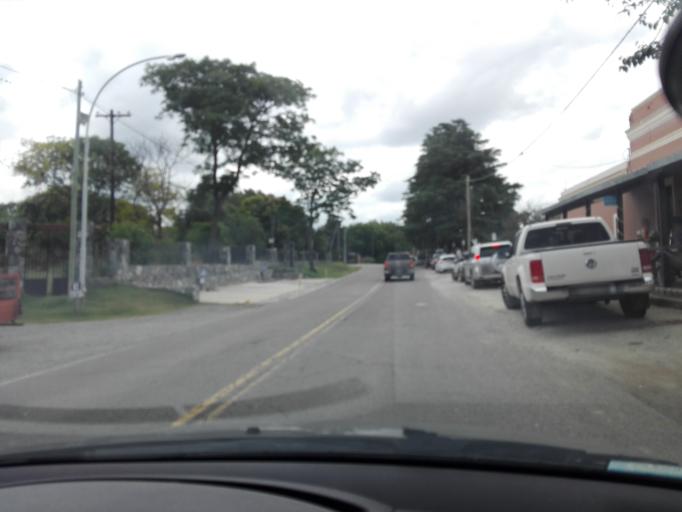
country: AR
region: Cordoba
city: Alta Gracia
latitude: -31.5877
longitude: -64.4593
